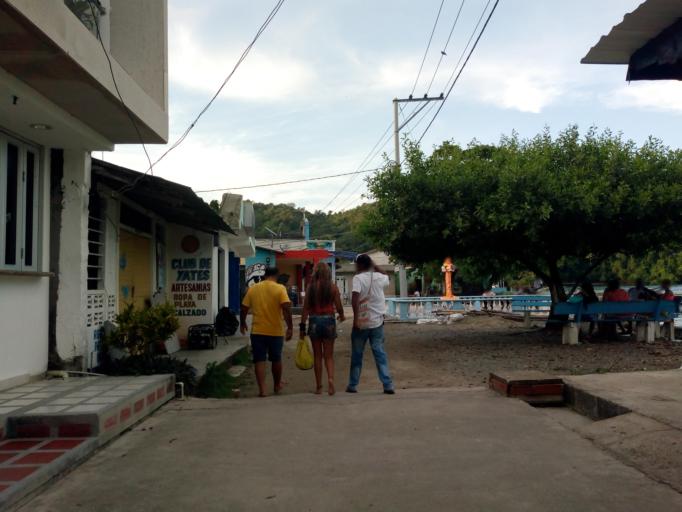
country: PA
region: Guna Yala
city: Puerto Obaldia
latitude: 8.6600
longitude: -77.3657
